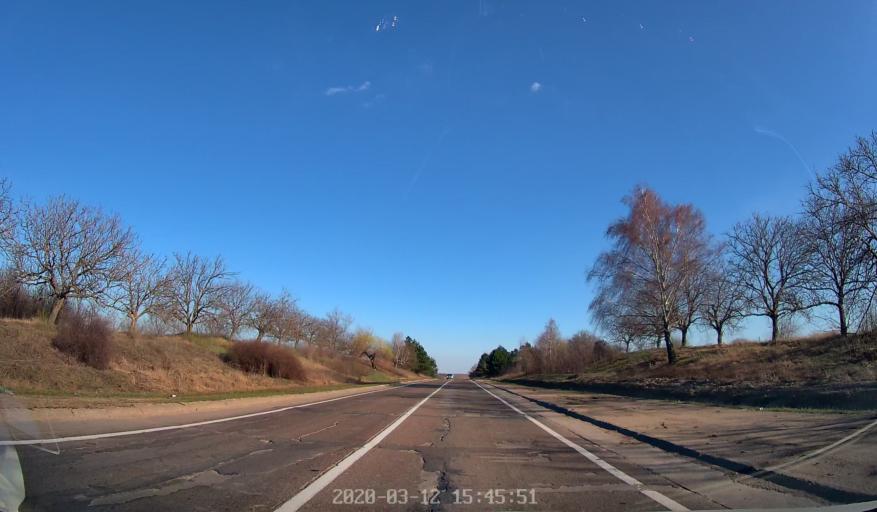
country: MD
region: Chisinau
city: Stauceni
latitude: 47.1033
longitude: 28.8824
